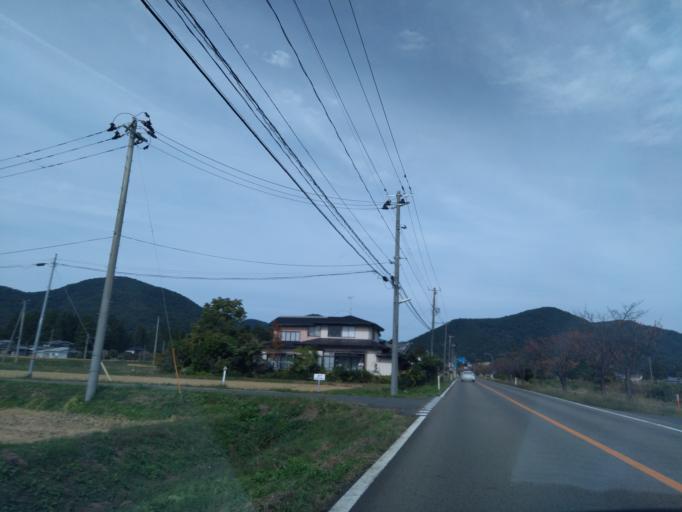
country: JP
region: Iwate
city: Hanamaki
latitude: 39.4415
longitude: 141.0772
